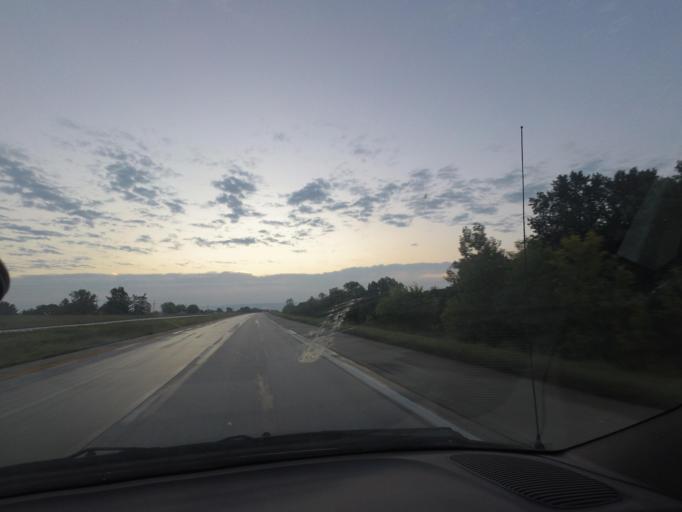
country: US
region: Missouri
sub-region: Macon County
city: Macon
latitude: 39.7604
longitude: -92.5836
